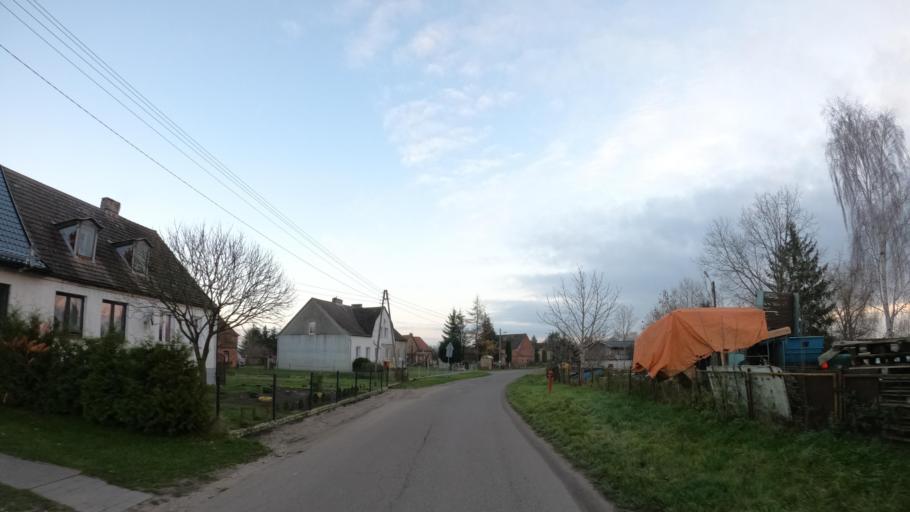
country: PL
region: West Pomeranian Voivodeship
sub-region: Powiat bialogardzki
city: Karlino
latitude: 54.0786
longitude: 15.8816
